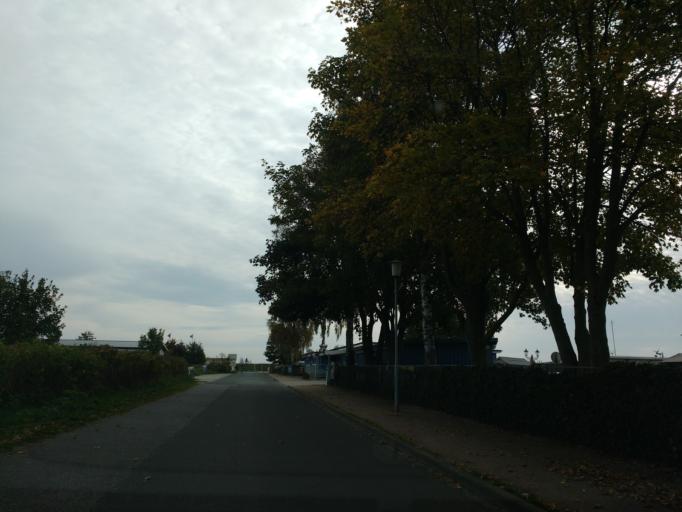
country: DE
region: Schleswig-Holstein
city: Gromitz
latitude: 54.1637
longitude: 11.0059
